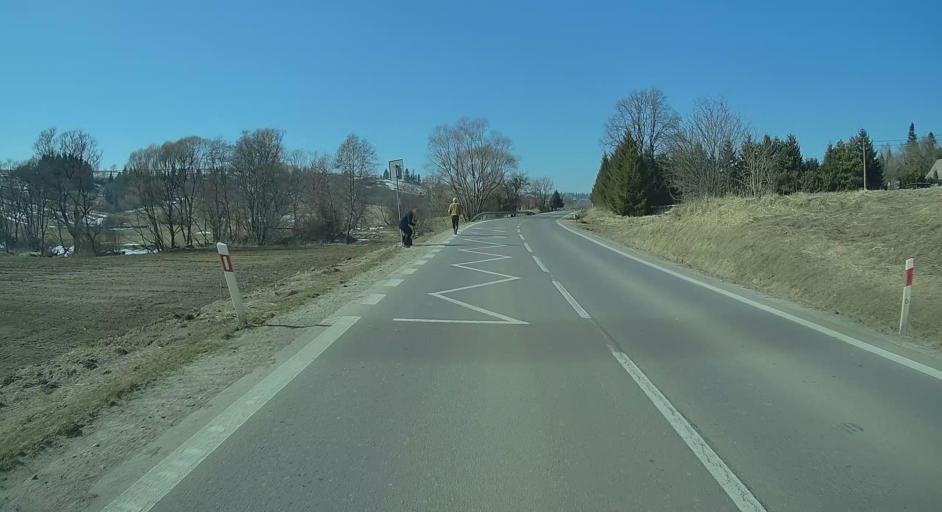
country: PL
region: Subcarpathian Voivodeship
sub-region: Powiat bieszczadzki
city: Ustrzyki Dolne
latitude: 49.5001
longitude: 22.6309
